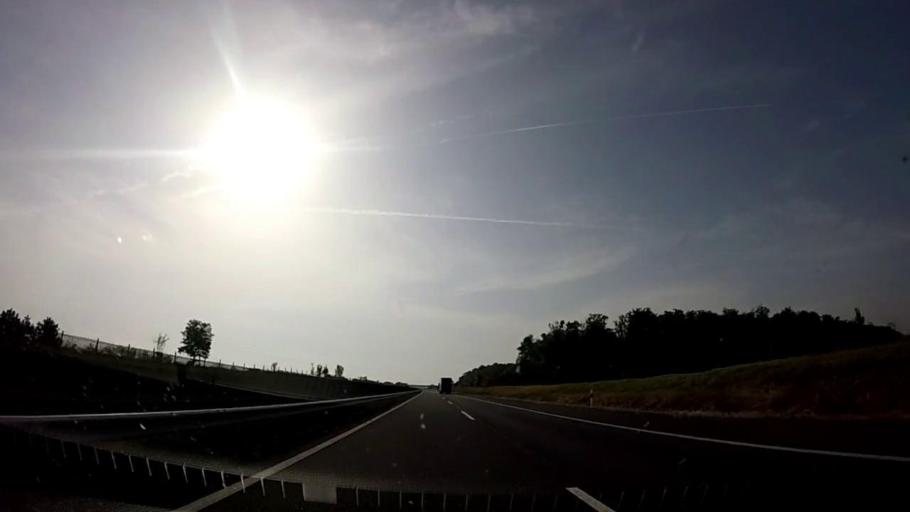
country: HU
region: Zala
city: Zalakomar
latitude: 46.5942
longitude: 17.2509
